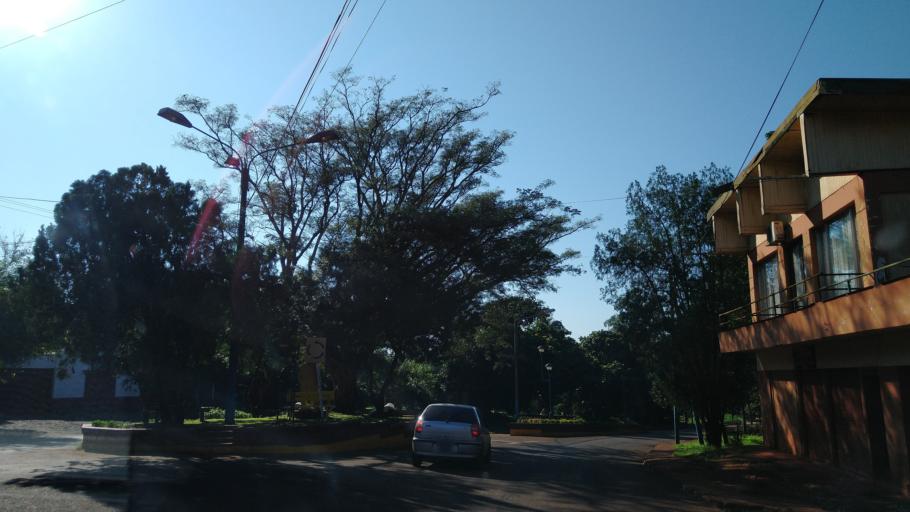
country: AR
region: Misiones
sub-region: Departamento de Montecarlo
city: Montecarlo
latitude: -26.5617
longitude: -54.7757
